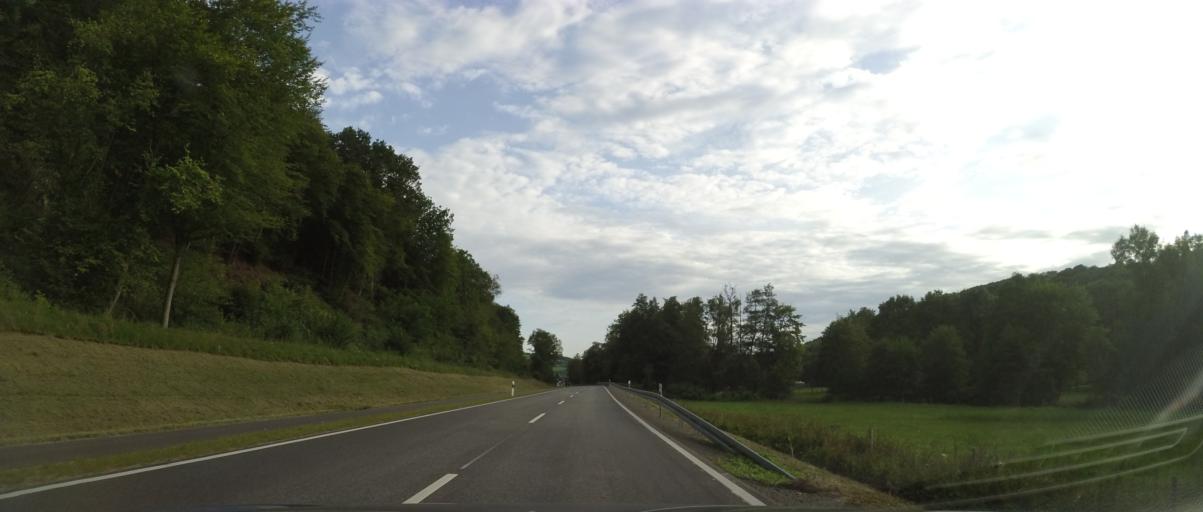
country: DE
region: Saarland
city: Nonnweiler
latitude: 49.5473
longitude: 6.9740
